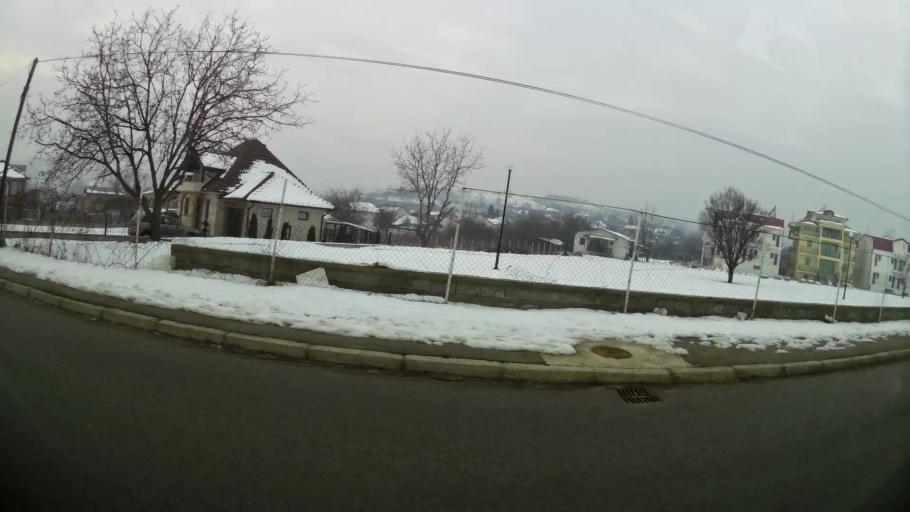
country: MK
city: Kondovo
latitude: 42.0342
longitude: 21.3433
